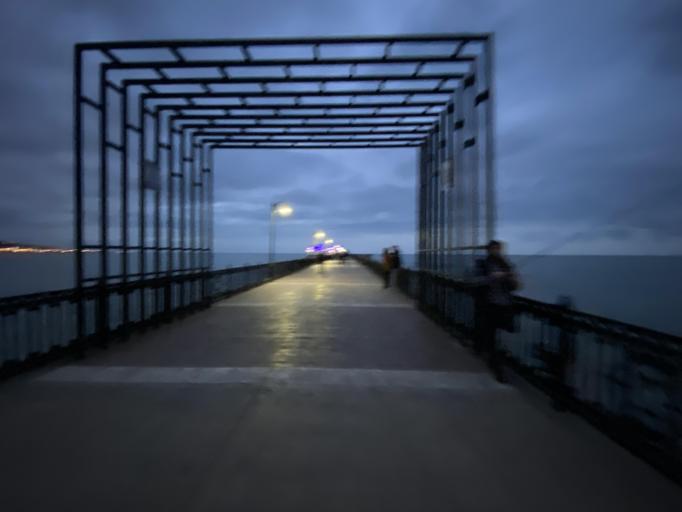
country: TR
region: Samsun
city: Samsun
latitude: 41.3439
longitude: 36.2619
